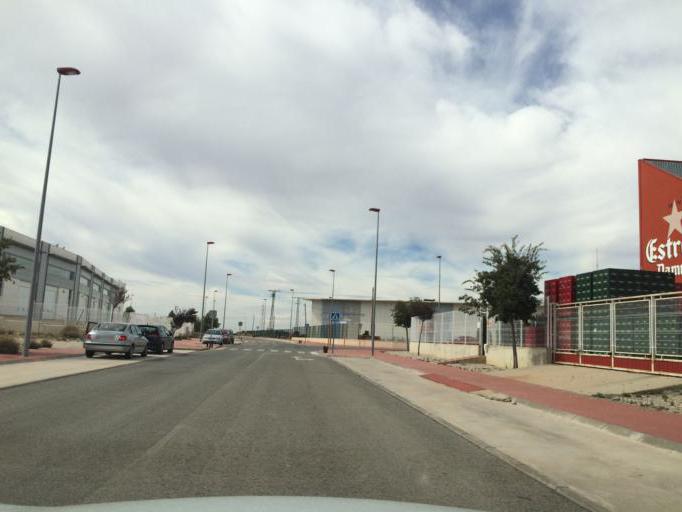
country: ES
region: Castille-La Mancha
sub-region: Provincia de Albacete
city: Albacete
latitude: 39.0301
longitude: -1.8900
